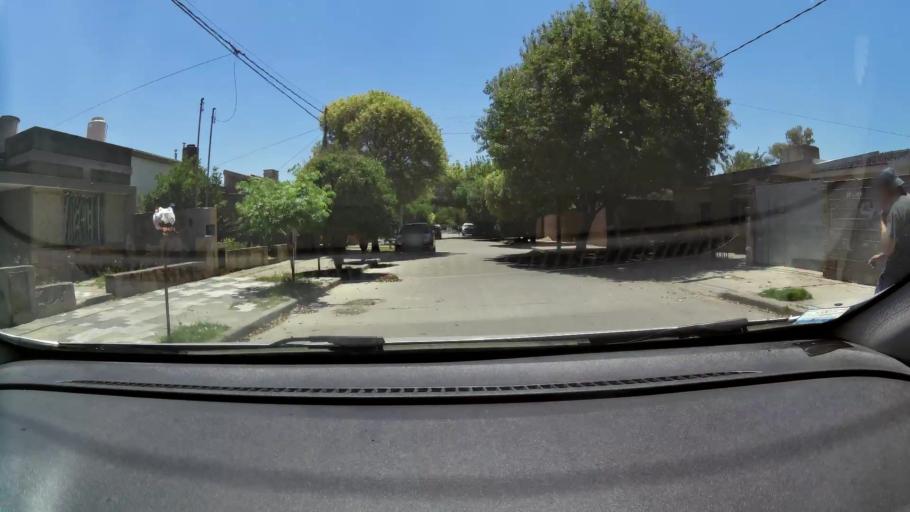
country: AR
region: Cordoba
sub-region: Departamento de Capital
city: Cordoba
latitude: -31.3842
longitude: -64.1304
